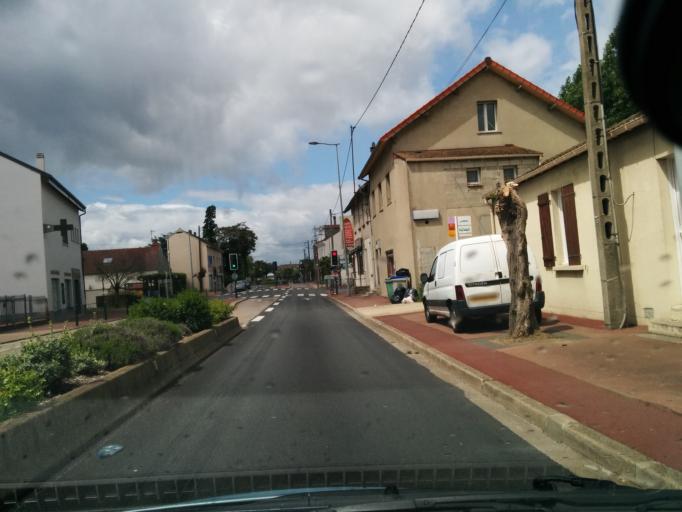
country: FR
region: Ile-de-France
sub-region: Departement des Yvelines
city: Porcheville
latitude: 48.9717
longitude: 1.7801
